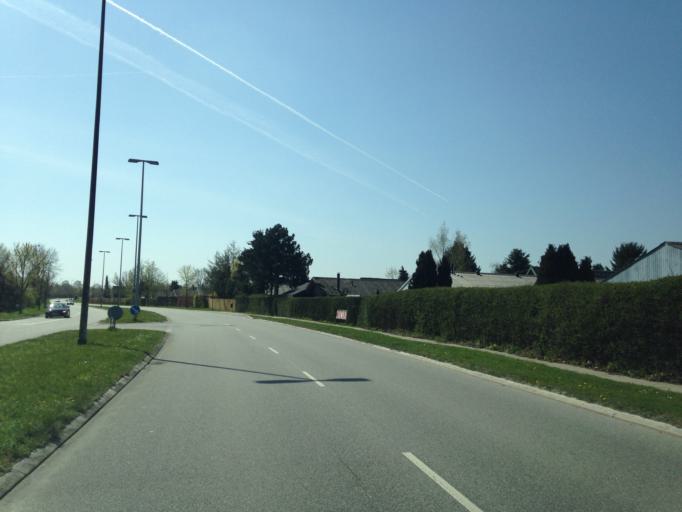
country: DK
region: Zealand
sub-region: Greve Kommune
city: Greve
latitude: 55.5861
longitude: 12.2703
